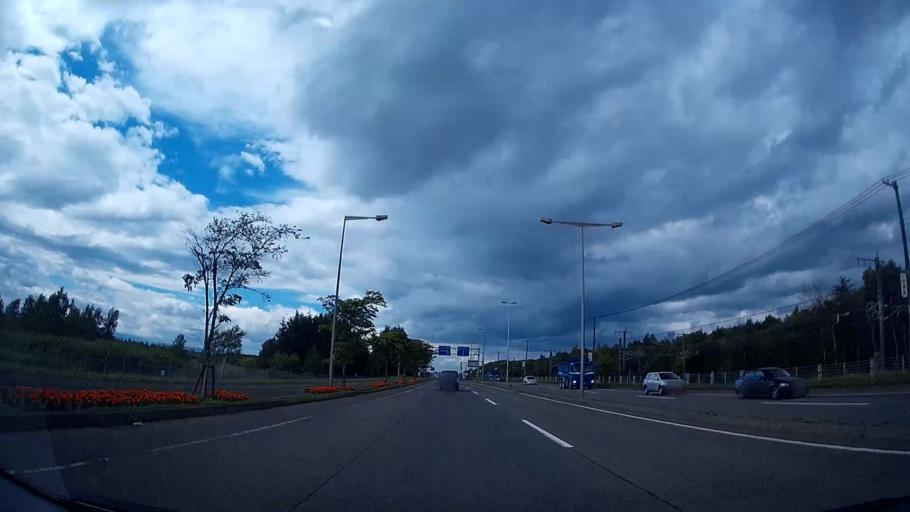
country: JP
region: Hokkaido
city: Chitose
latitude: 42.8137
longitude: 141.6681
